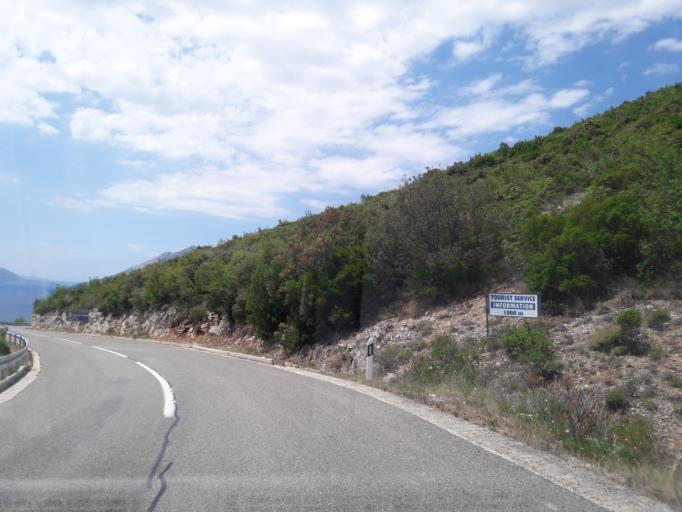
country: HR
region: Dubrovacko-Neretvanska
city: Orebic
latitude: 42.9698
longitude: 17.2524
